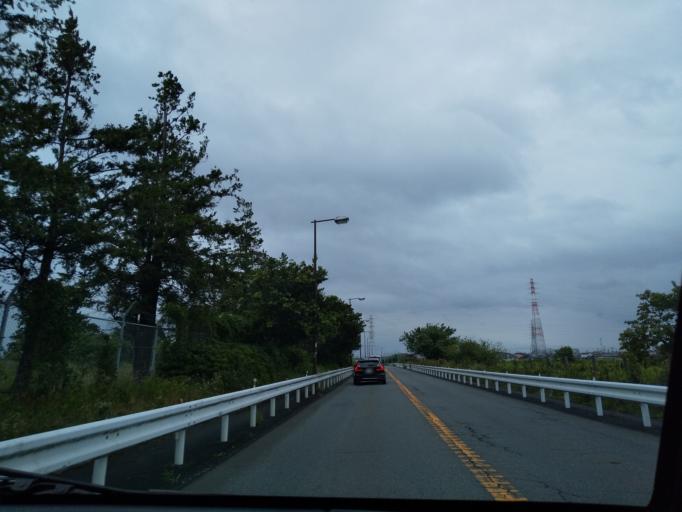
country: JP
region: Kanagawa
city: Fujisawa
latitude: 35.3993
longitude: 139.5031
